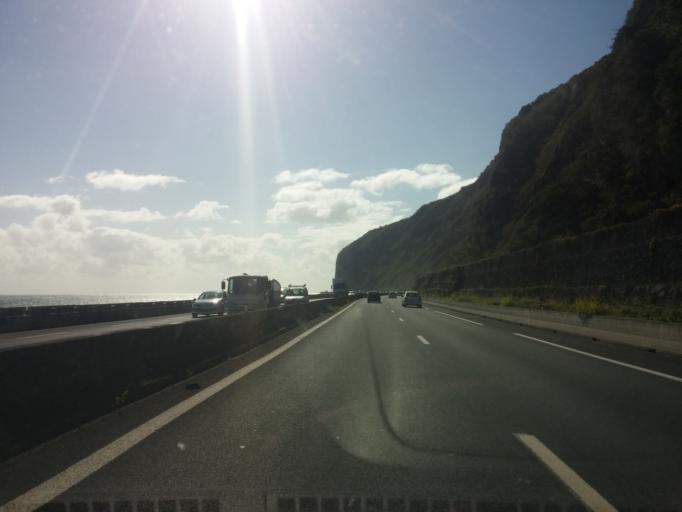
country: RE
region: Reunion
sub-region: Reunion
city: La Possession
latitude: -20.8904
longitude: 55.3855
